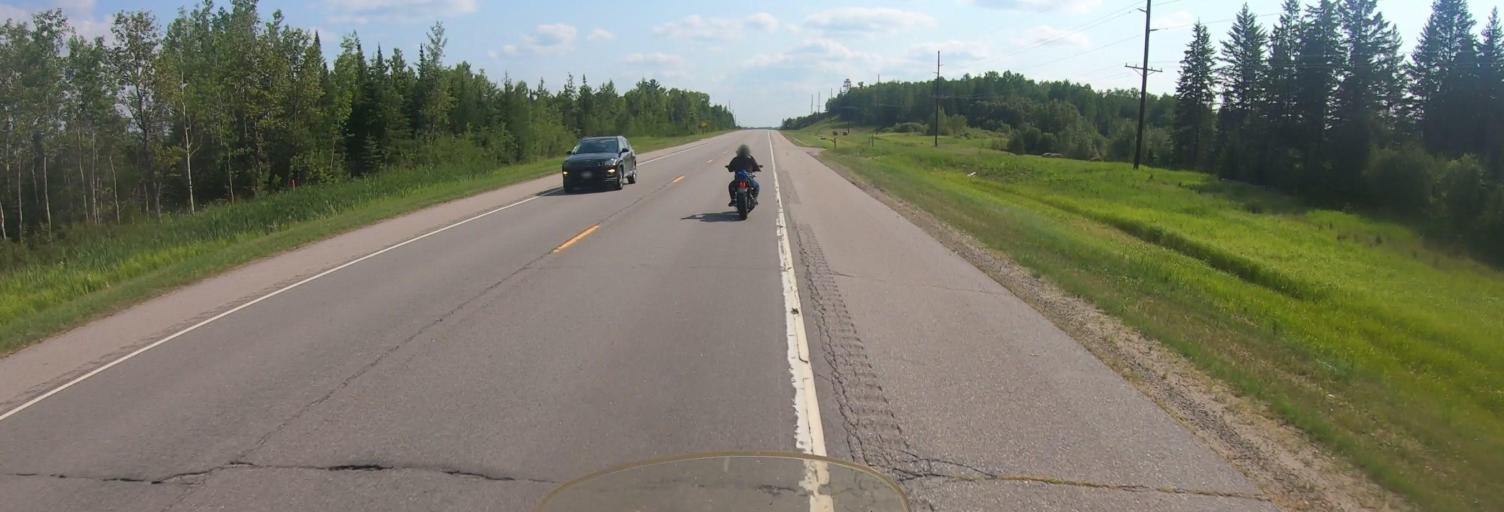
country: US
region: Minnesota
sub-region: Saint Louis County
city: Chisholm
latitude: 47.9589
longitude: -92.8296
